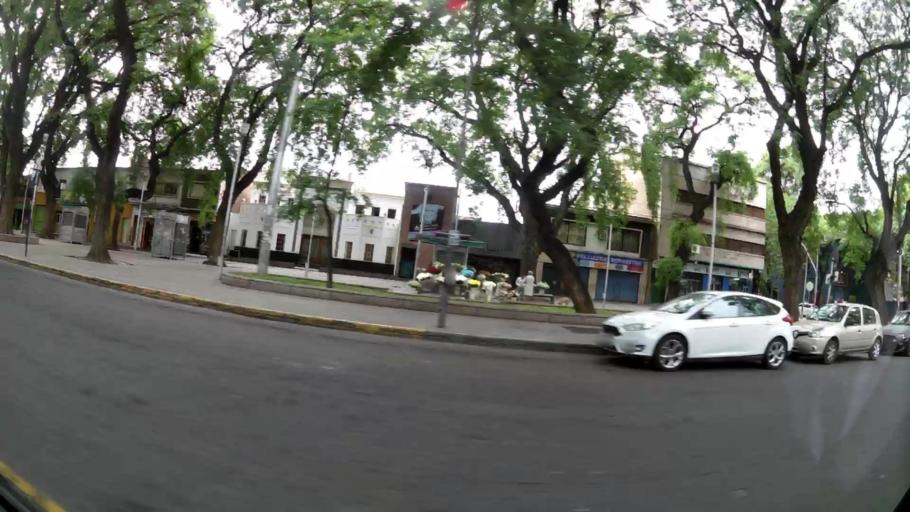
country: AR
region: Mendoza
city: Mendoza
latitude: -32.8806
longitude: -68.8368
